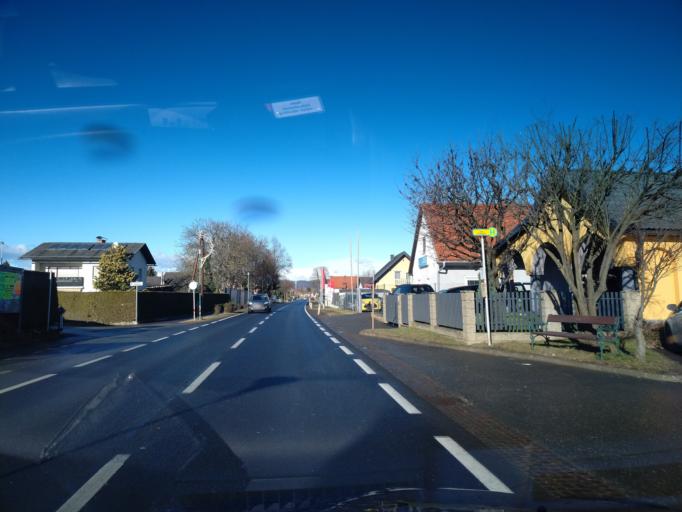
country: AT
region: Styria
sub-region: Politischer Bezirk Leibnitz
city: Kaindorf an der Sulm
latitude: 46.8073
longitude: 15.5519
